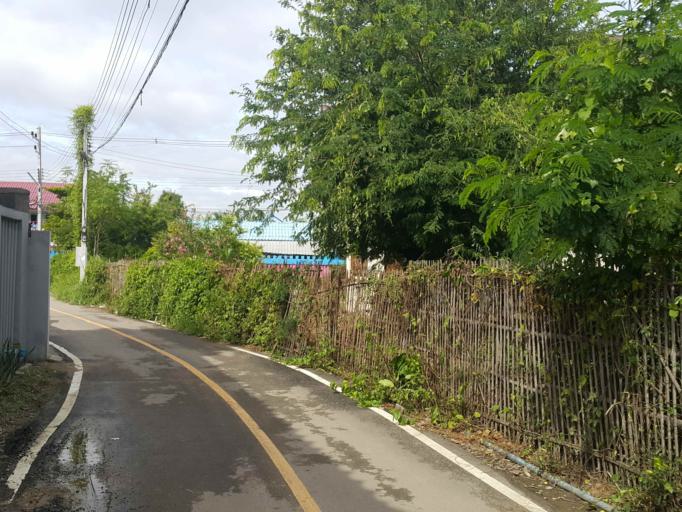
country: TH
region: Chiang Mai
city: San Kamphaeng
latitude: 18.7645
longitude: 99.0726
